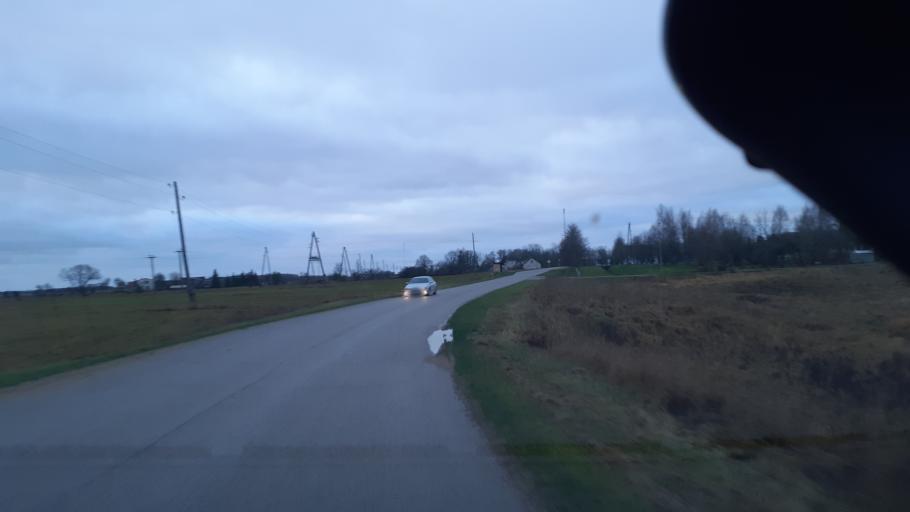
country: LV
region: Alsunga
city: Alsunga
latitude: 56.8876
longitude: 21.6061
